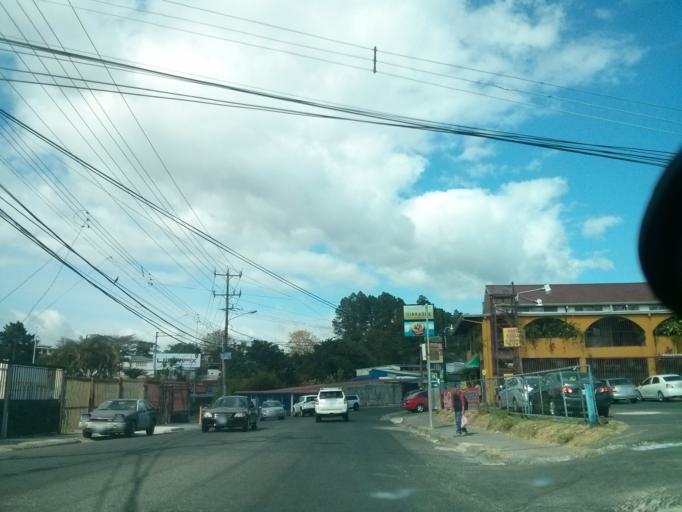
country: CR
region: San Jose
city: Curridabat
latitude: 9.9077
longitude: -84.0412
